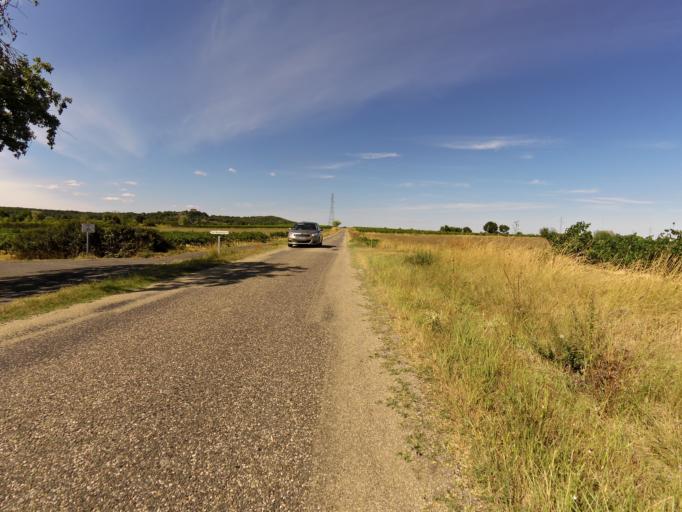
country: FR
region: Languedoc-Roussillon
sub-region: Departement du Gard
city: Lezan
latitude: 43.9666
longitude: 4.0254
